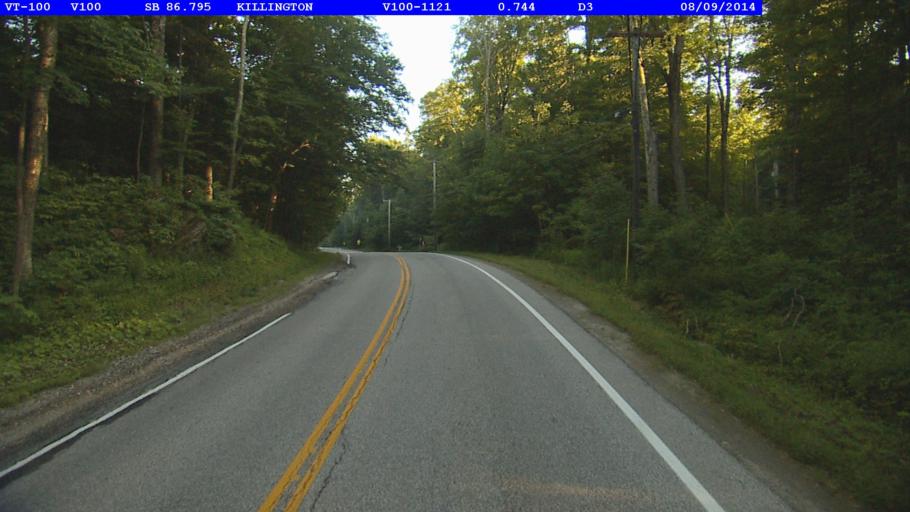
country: US
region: Vermont
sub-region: Rutland County
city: Rutland
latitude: 43.6775
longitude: -72.8105
